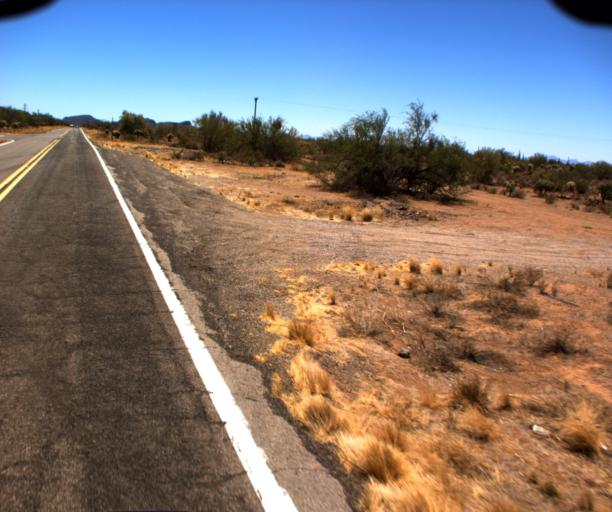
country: US
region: Arizona
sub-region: Pima County
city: Sells
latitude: 32.0146
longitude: -111.9969
